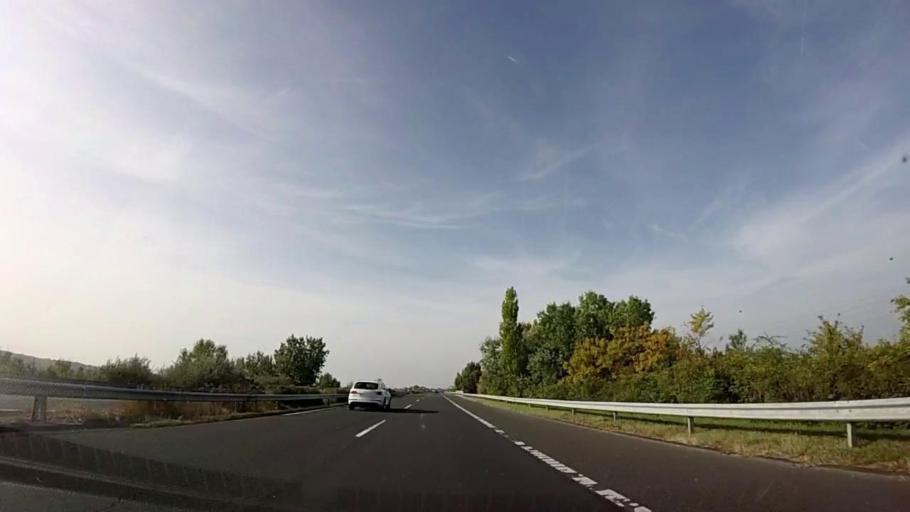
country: HU
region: Somogy
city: Siofok
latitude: 46.9051
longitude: 18.0829
